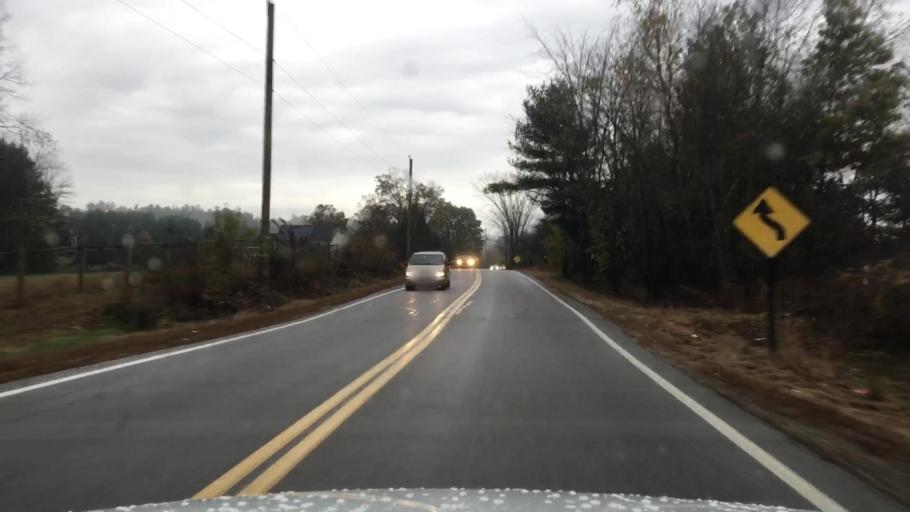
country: US
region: Maine
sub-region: York County
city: Berwick
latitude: 43.2879
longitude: -70.9025
